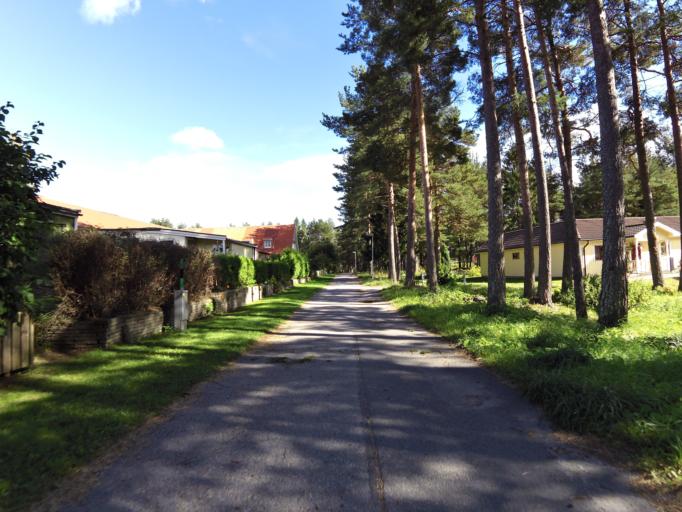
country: SE
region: Gaevleborg
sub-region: Gavle Kommun
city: Gavle
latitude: 60.6686
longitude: 17.2199
